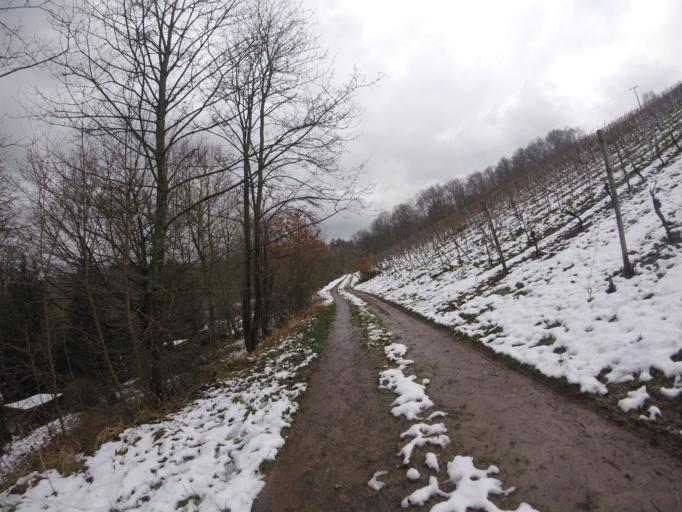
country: DE
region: Baden-Wuerttemberg
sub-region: Regierungsbezirk Stuttgart
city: Oberstenfeld
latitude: 48.9958
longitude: 9.3476
